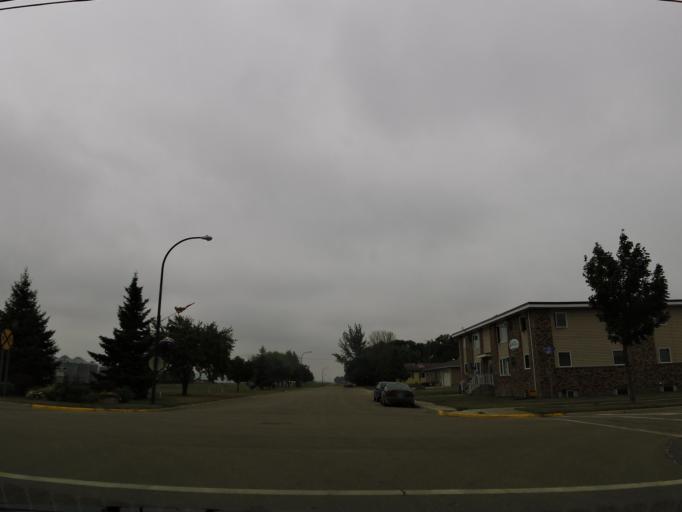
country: US
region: Minnesota
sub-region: Marshall County
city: Warren
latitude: 48.3328
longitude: -96.8188
